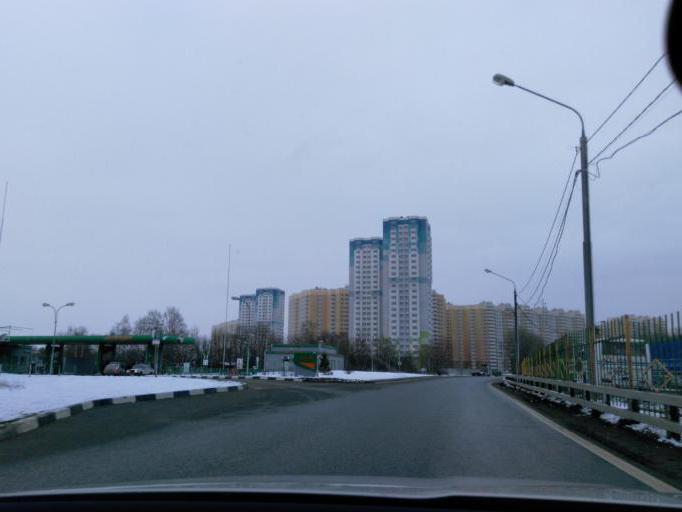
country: RU
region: Moskovskaya
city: Novopodrezkovo
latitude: 55.9521
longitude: 37.3452
